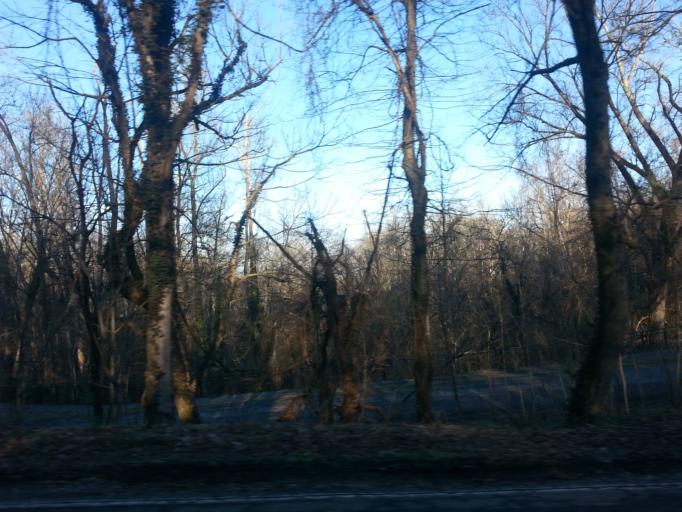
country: US
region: Tennessee
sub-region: Knox County
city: Knoxville
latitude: 35.9559
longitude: -83.8701
